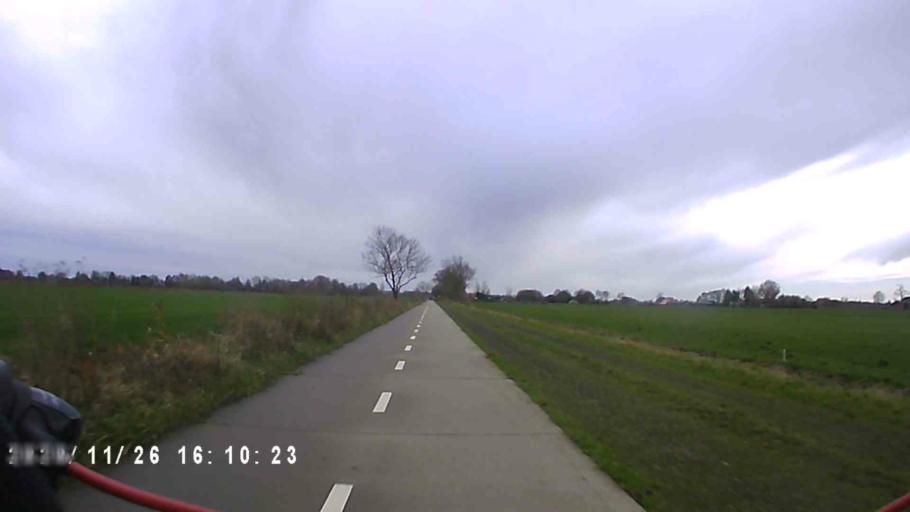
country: NL
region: Groningen
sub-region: Gemeente Bedum
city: Bedum
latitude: 53.2542
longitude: 6.6537
